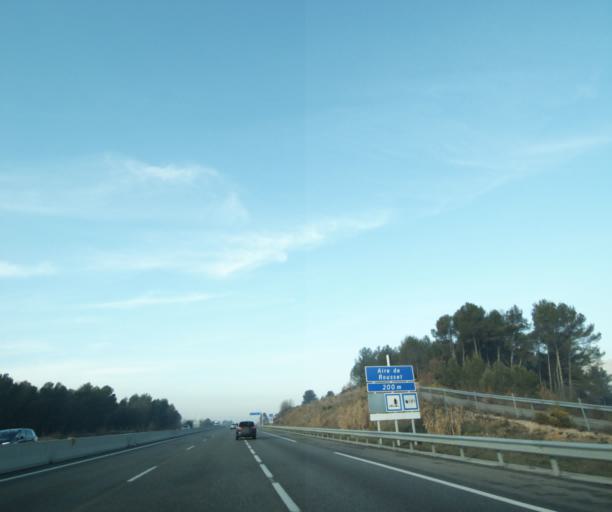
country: FR
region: Provence-Alpes-Cote d'Azur
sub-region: Departement des Bouches-du-Rhone
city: Peynier
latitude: 43.4702
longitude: 5.6507
